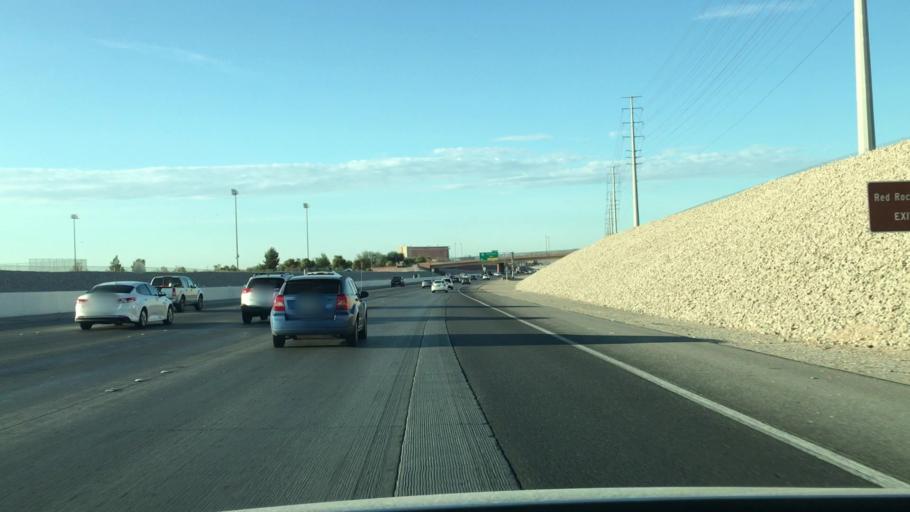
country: US
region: Nevada
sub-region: Clark County
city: Summerlin South
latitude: 36.1744
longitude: -115.3385
